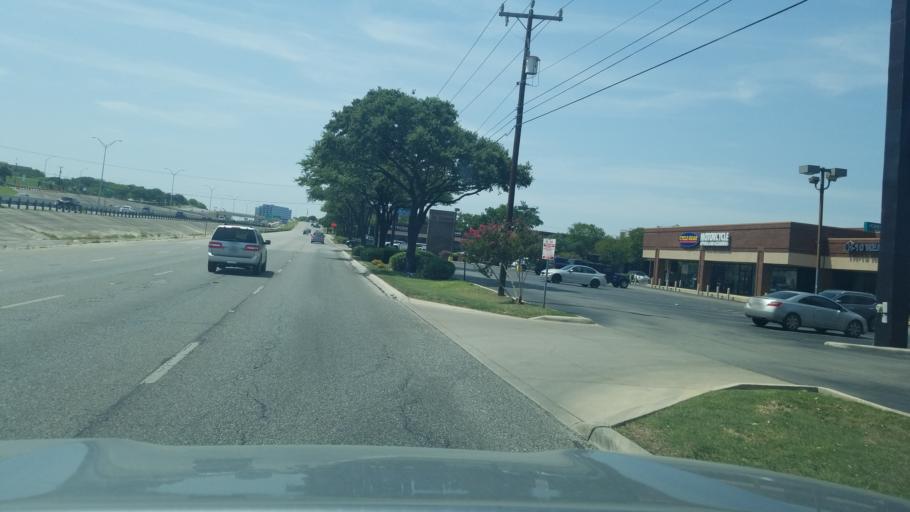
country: US
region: Texas
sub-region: Bexar County
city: Balcones Heights
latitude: 29.5355
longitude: -98.5661
